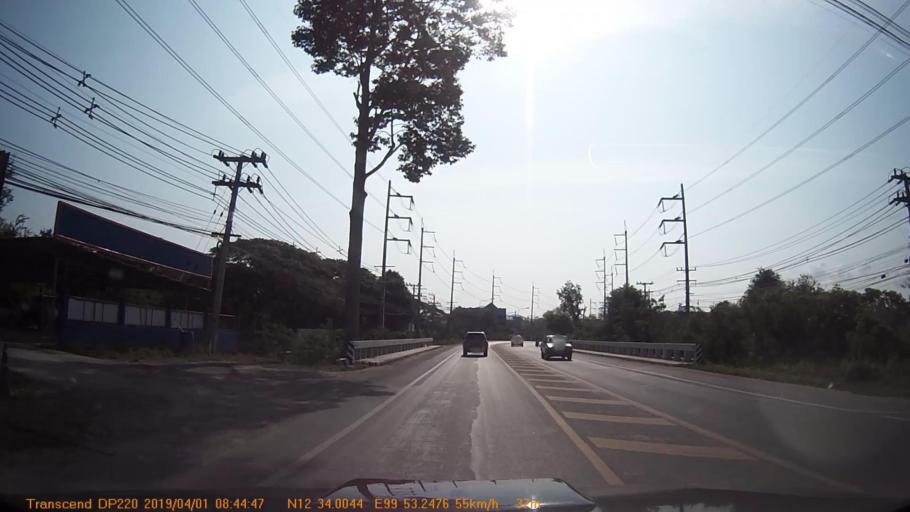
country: TH
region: Prachuap Khiri Khan
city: Hua Hin
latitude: 12.5668
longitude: 99.8877
